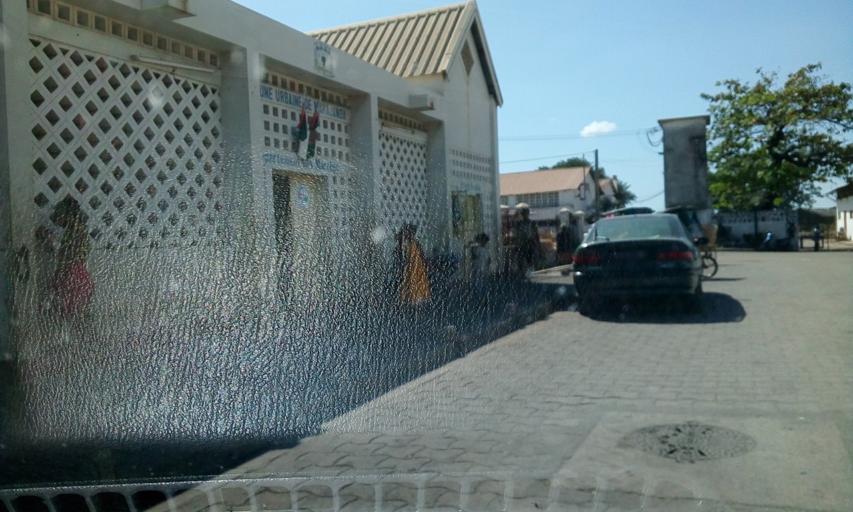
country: MG
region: Boeny
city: Mahajanga
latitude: -15.7255
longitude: 46.3181
